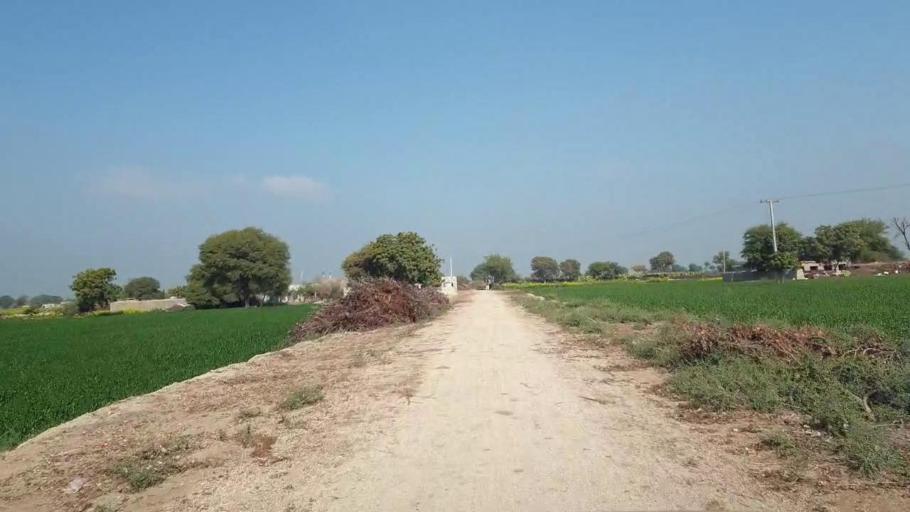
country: PK
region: Sindh
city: Shahdadpur
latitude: 26.0242
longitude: 68.5845
